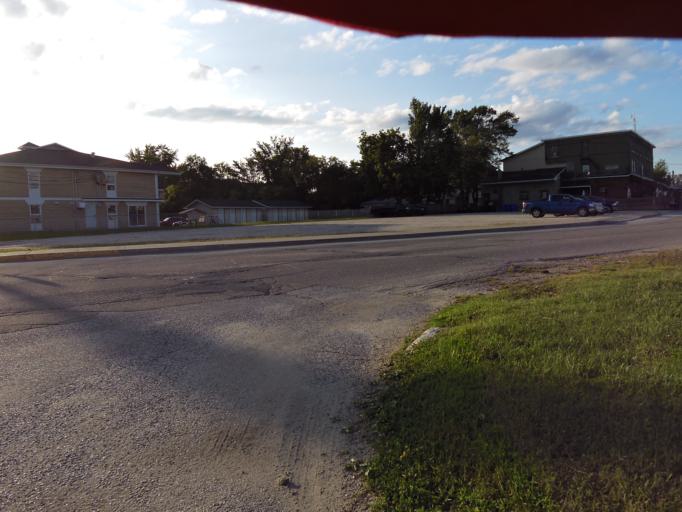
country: CA
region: Quebec
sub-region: Outaouais
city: Maniwaki
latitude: 46.3740
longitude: -75.9766
